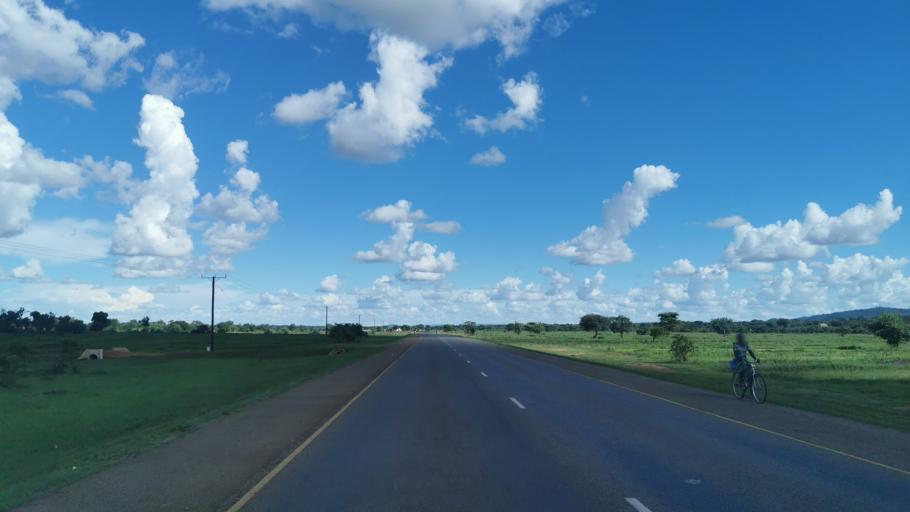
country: TZ
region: Geita
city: Ushirombo
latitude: -3.4784
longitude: 31.9185
